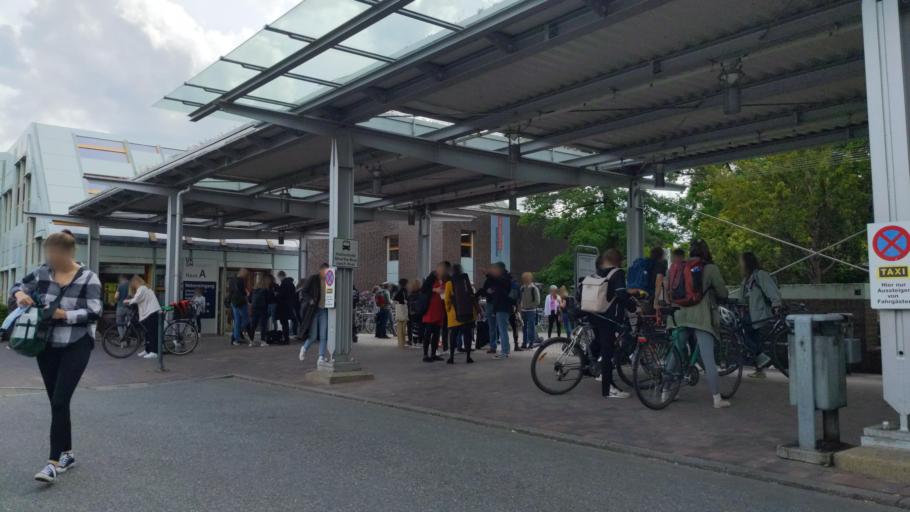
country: DE
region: Schleswig-Holstein
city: Luebeck
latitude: 53.8357
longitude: 10.7057
